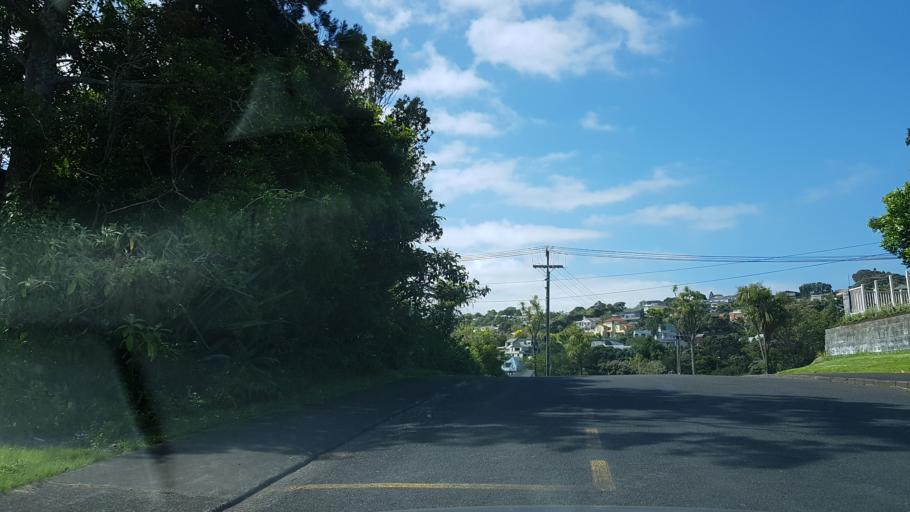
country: NZ
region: Auckland
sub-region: Auckland
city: North Shore
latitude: -36.8108
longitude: 174.6908
